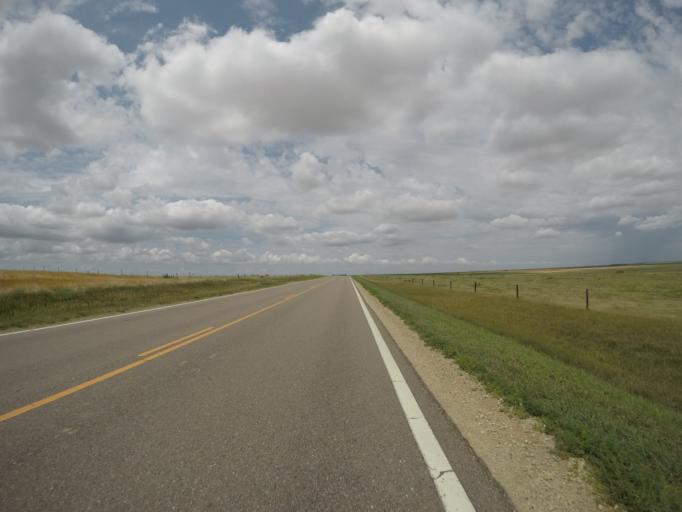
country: US
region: Kansas
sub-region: Rawlins County
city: Atwood
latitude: 39.6917
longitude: -101.0564
